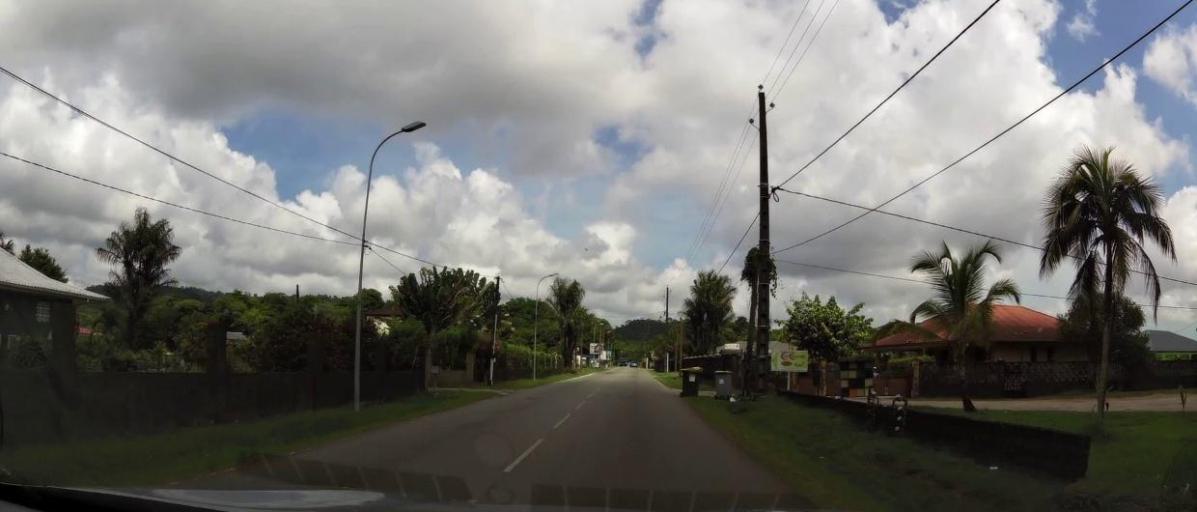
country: GF
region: Guyane
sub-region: Guyane
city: Matoury
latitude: 4.8751
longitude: -52.3333
